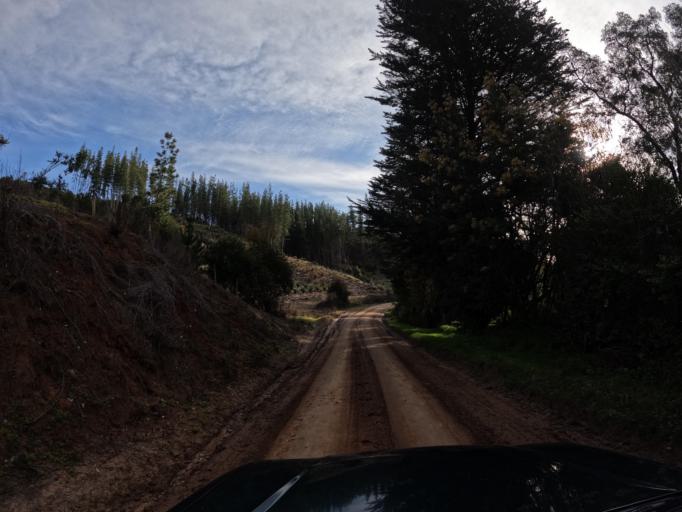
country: CL
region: Biobio
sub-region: Provincia de Biobio
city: La Laja
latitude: -37.1954
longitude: -72.7532
